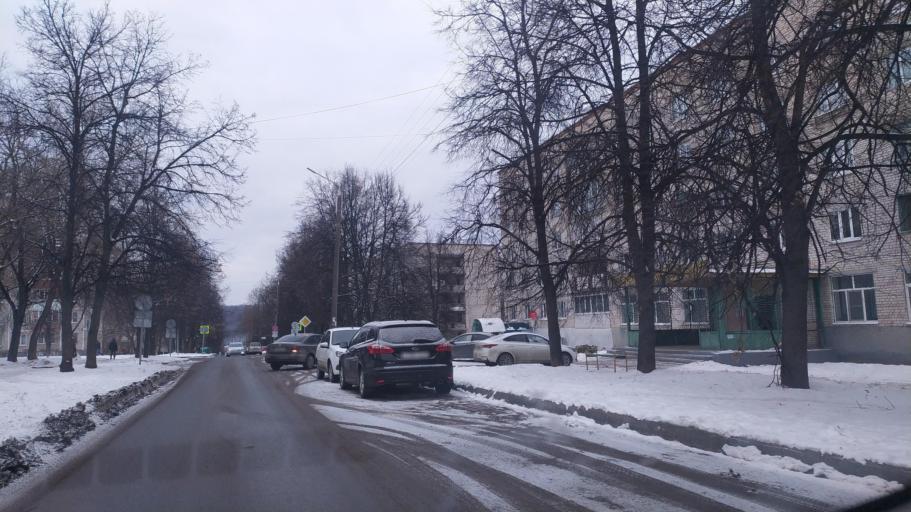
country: RU
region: Chuvashia
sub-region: Cheboksarskiy Rayon
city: Cheboksary
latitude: 56.1244
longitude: 47.1993
